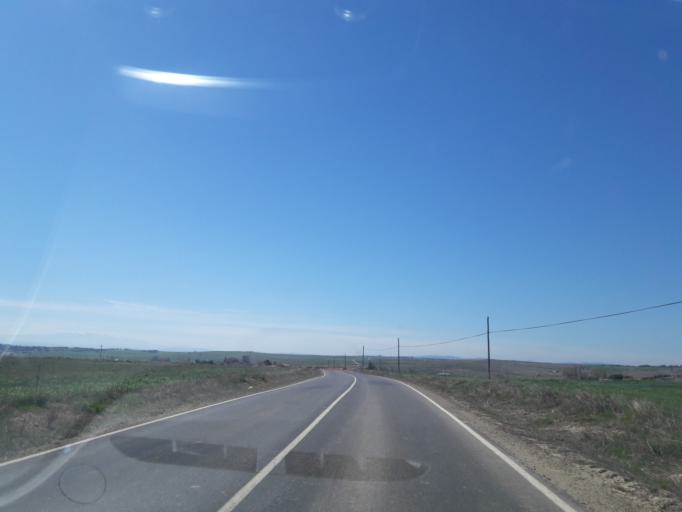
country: ES
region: Castille and Leon
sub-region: Provincia de Salamanca
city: Martinamor
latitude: 40.8112
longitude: -5.5959
